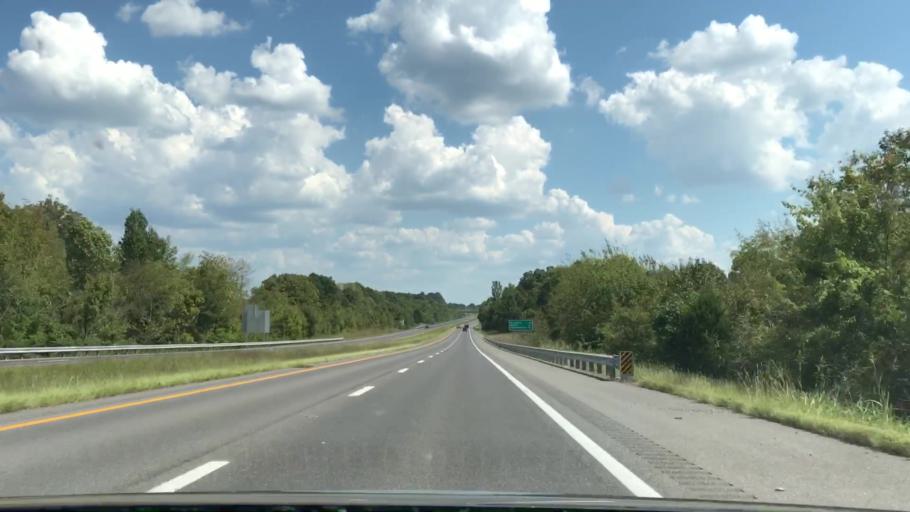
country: US
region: Kentucky
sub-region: Lyon County
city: Eddyville
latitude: 37.1093
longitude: -88.0131
